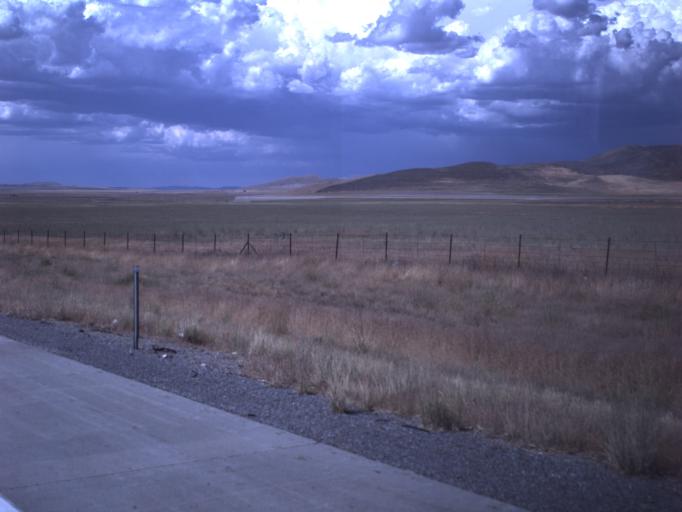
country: US
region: Utah
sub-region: Box Elder County
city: Garland
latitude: 41.8284
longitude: -112.4258
